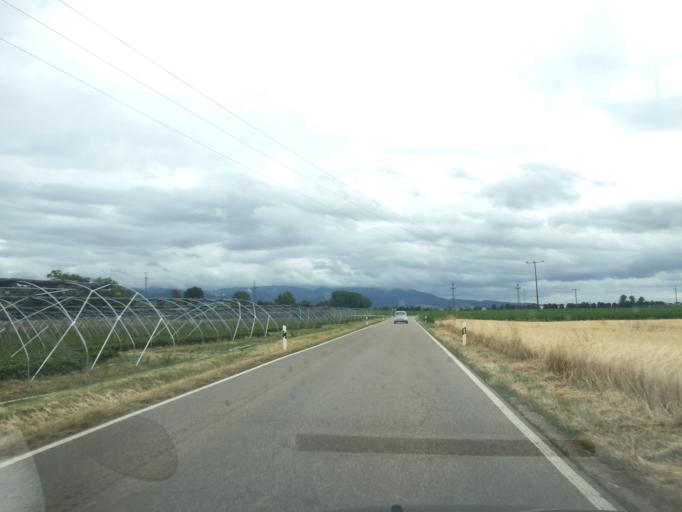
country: DE
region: Baden-Wuerttemberg
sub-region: Freiburg Region
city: Unterkrozingen
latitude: 47.9213
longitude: 7.6735
